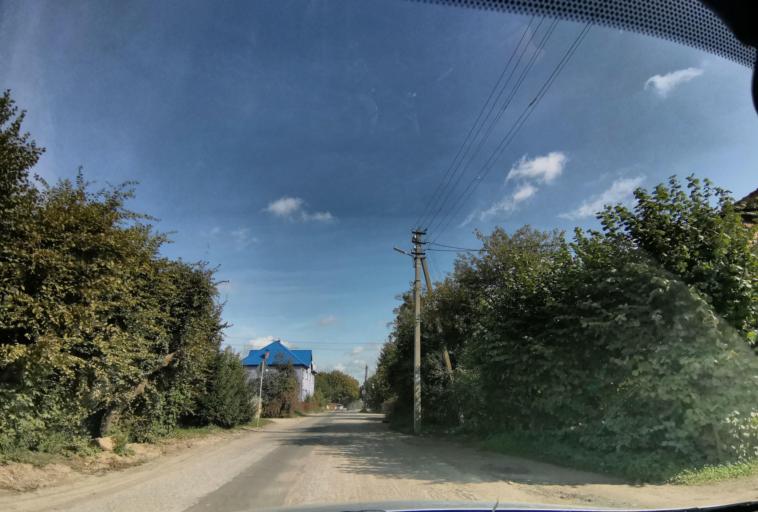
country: RU
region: Kaliningrad
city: Chernyakhovsk
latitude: 54.6606
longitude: 21.8378
